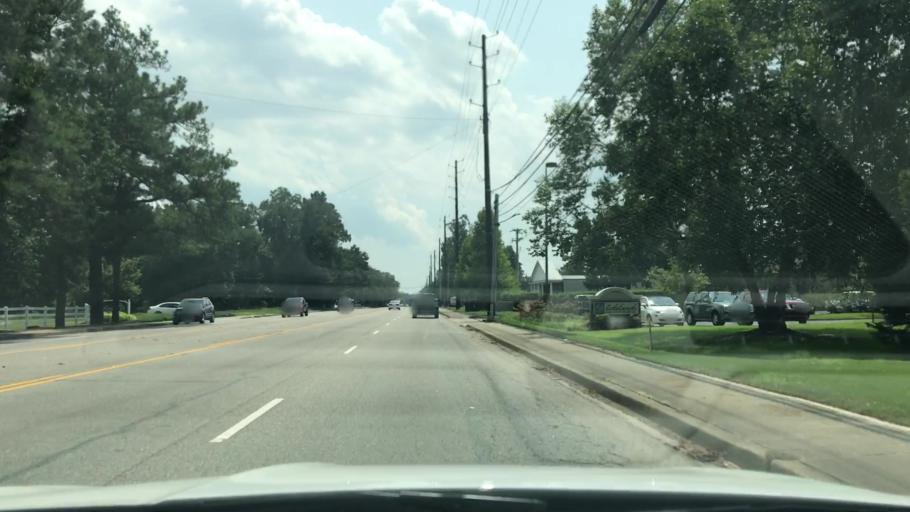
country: US
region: South Carolina
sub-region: Georgetown County
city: Georgetown
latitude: 33.4115
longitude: -79.2858
